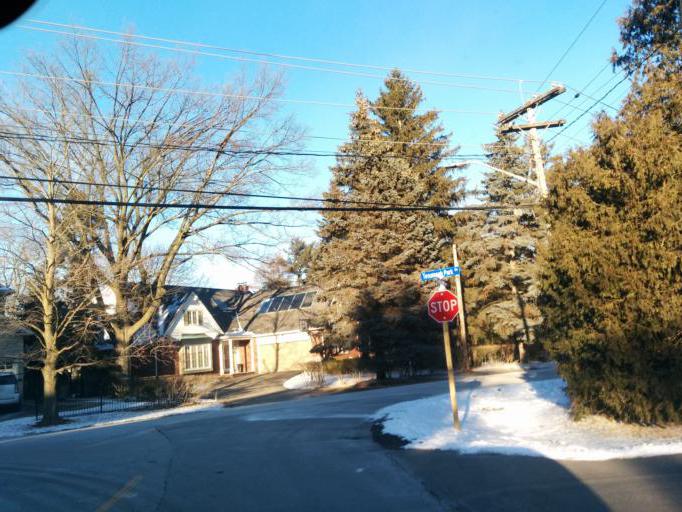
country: CA
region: Ontario
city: Mississauga
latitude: 43.5390
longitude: -79.6100
